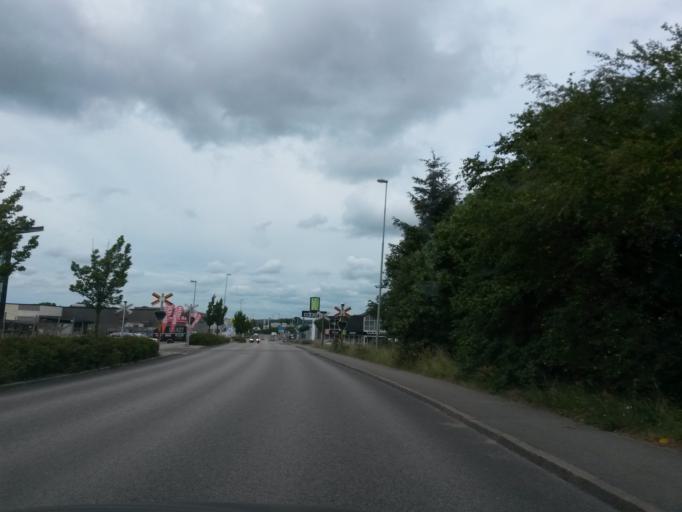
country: SE
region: Halland
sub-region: Varbergs Kommun
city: Varberg
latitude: 57.1201
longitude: 12.2611
